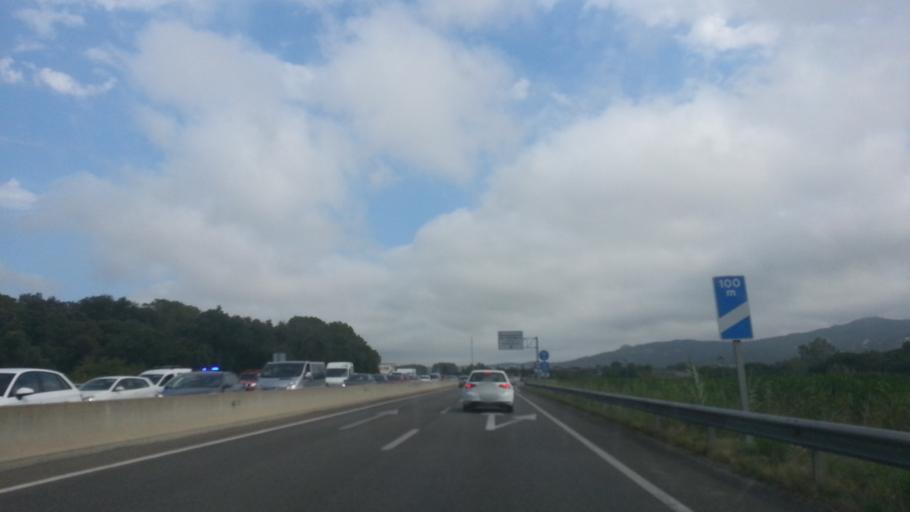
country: ES
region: Catalonia
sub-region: Provincia de Girona
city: Santa Cristina d'Aro
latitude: 41.8259
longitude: 2.9726
